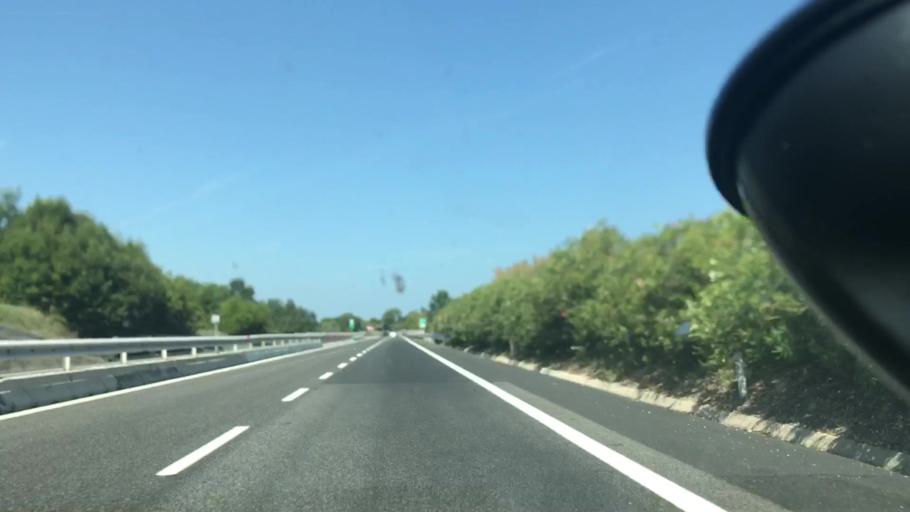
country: IT
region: Abruzzo
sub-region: Provincia di Chieti
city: Tollo
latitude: 42.3526
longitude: 14.3531
